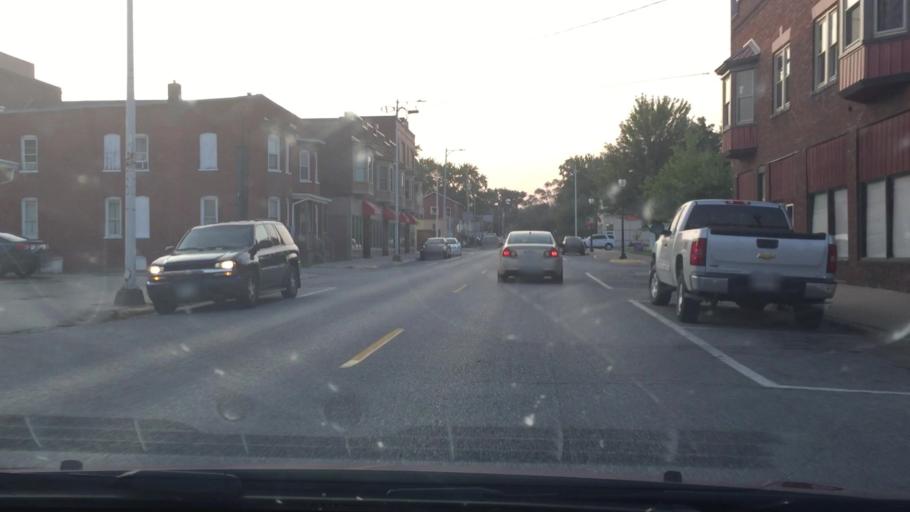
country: US
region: Iowa
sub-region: Muscatine County
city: Muscatine
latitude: 41.4262
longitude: -91.0439
